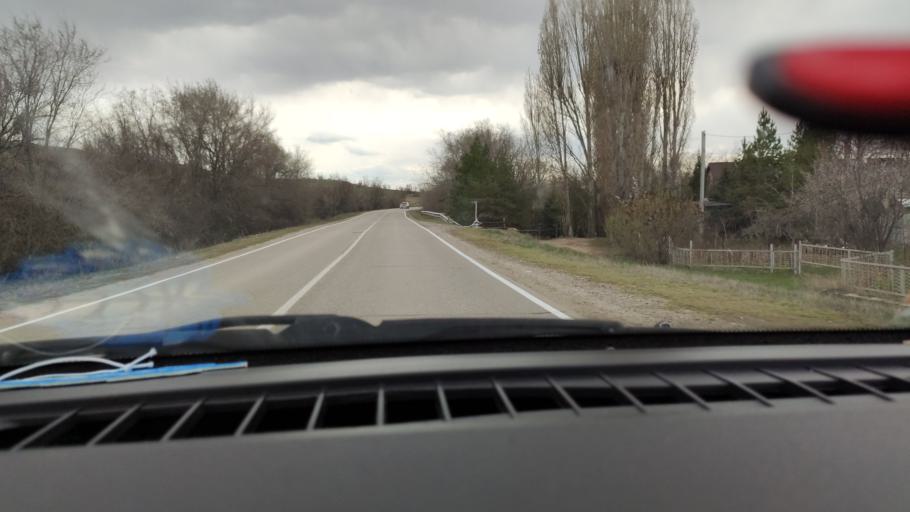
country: RU
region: Saratov
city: Privolzhskiy
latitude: 51.2189
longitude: 45.9188
